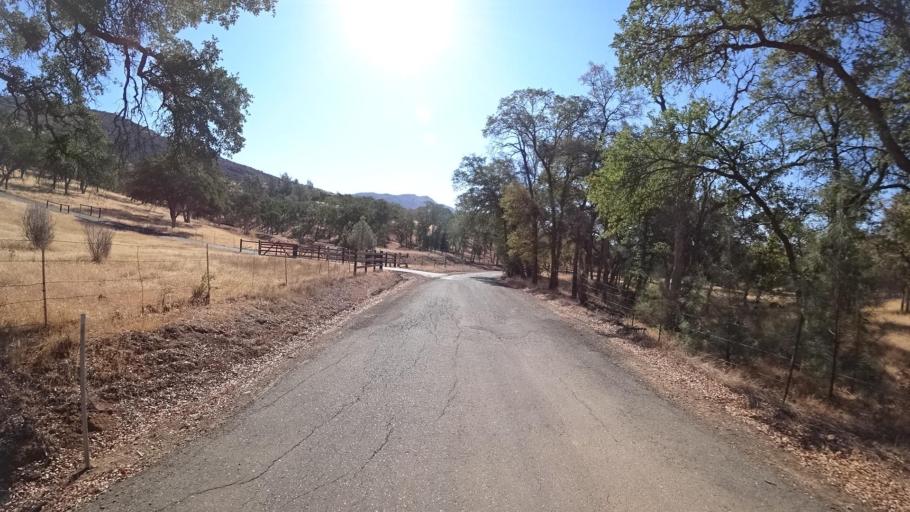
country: US
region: California
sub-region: Mariposa County
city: Mariposa
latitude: 37.6054
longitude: -120.2015
